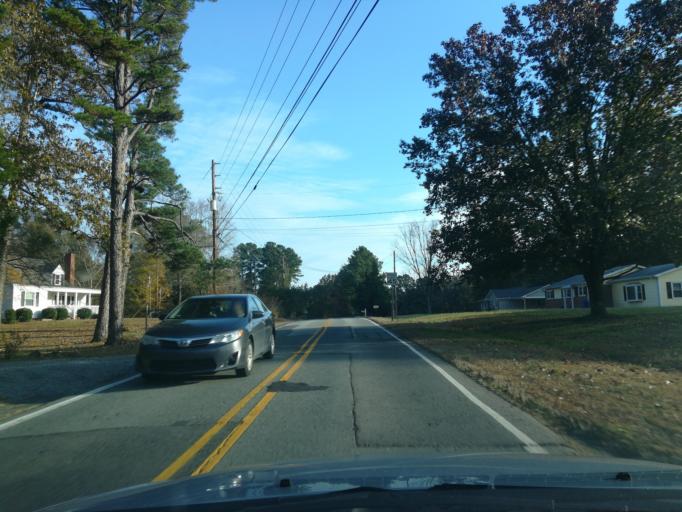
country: US
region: North Carolina
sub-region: Orange County
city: Chapel Hill
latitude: 35.9622
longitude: -79.0002
